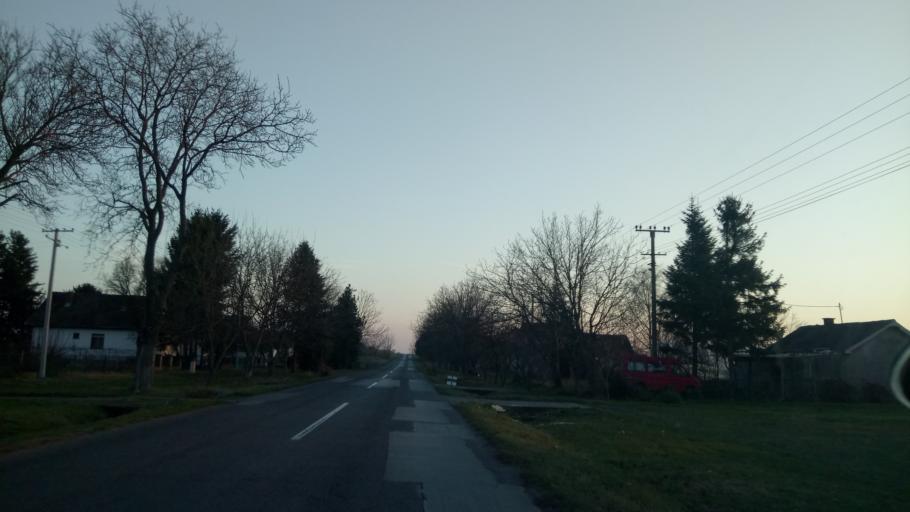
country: RS
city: Surduk
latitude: 45.0647
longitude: 20.3301
